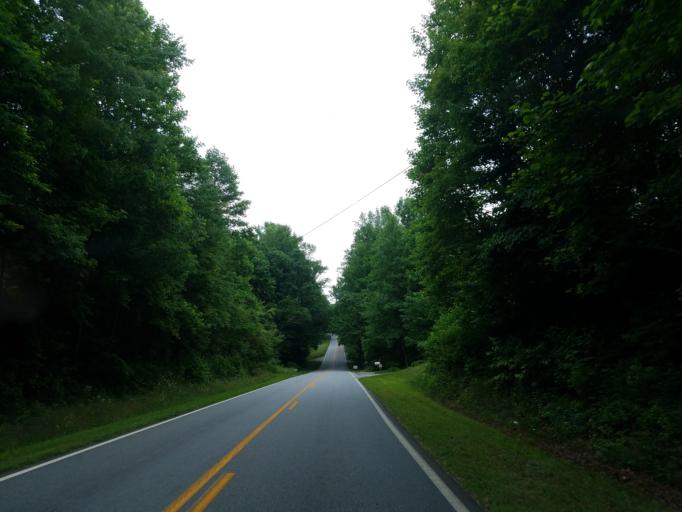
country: US
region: Georgia
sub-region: Lumpkin County
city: Dahlonega
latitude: 34.6126
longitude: -83.9749
